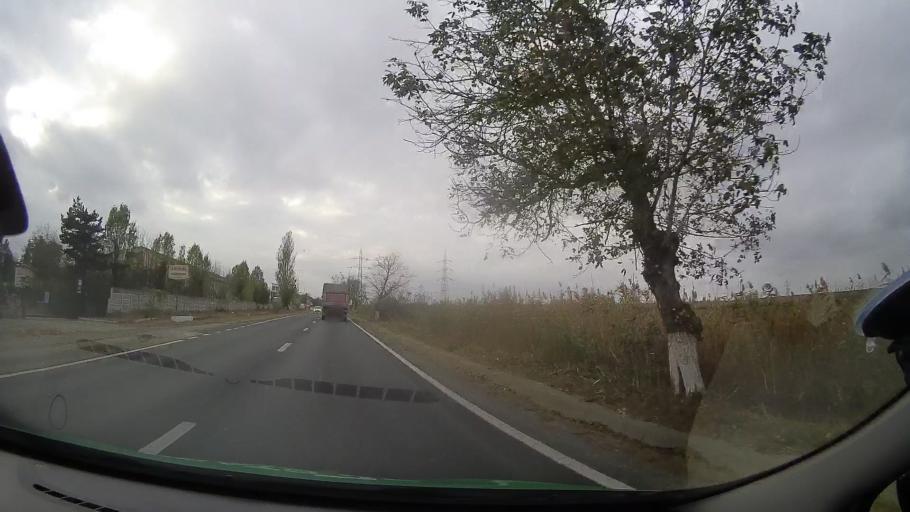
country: RO
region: Constanta
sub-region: Municipiul Medgidia
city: Medgidia
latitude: 44.2680
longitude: 28.2758
